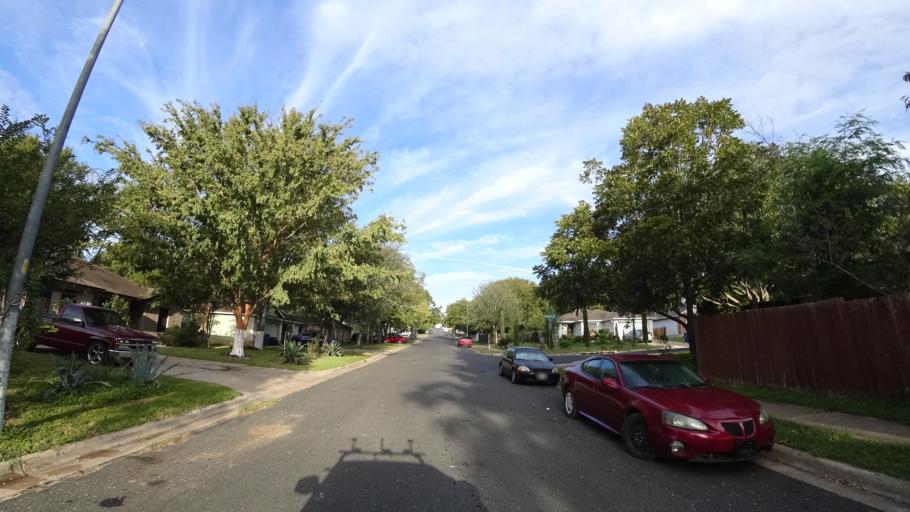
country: US
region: Texas
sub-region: Travis County
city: Onion Creek
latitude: 30.1891
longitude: -97.7359
